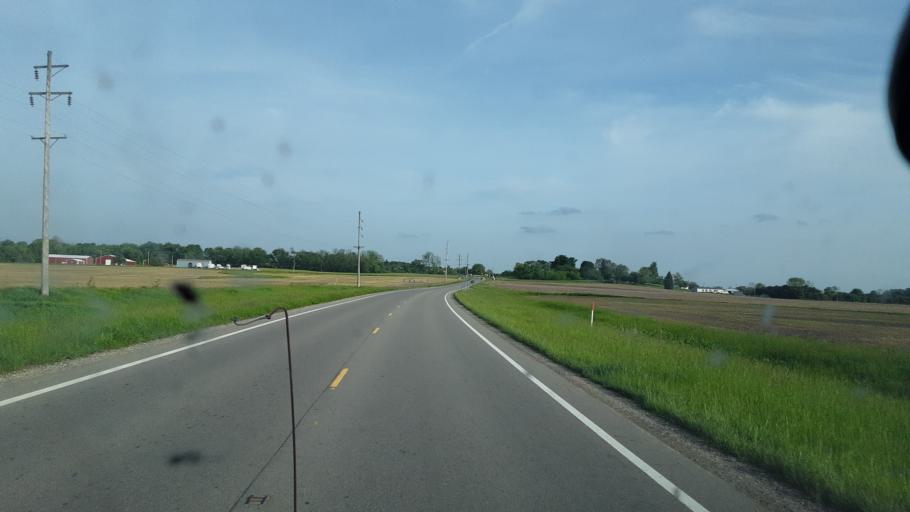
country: US
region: Ohio
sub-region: Ross County
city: Kingston
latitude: 39.5372
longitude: -82.8434
